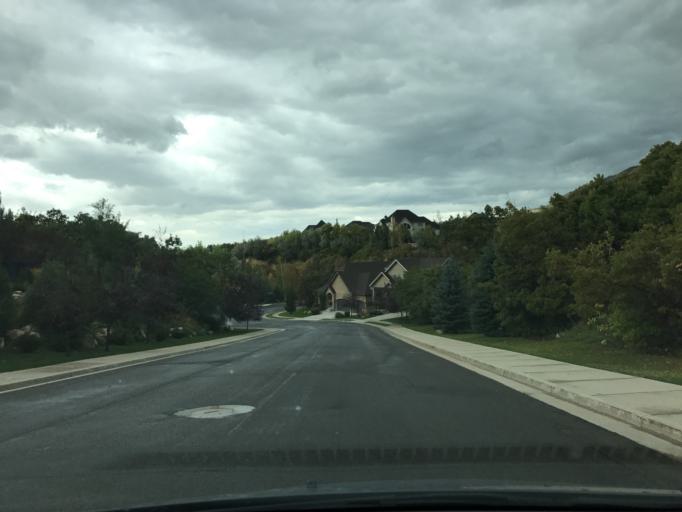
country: US
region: Utah
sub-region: Davis County
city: Fruit Heights
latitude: 41.0168
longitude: -111.8995
